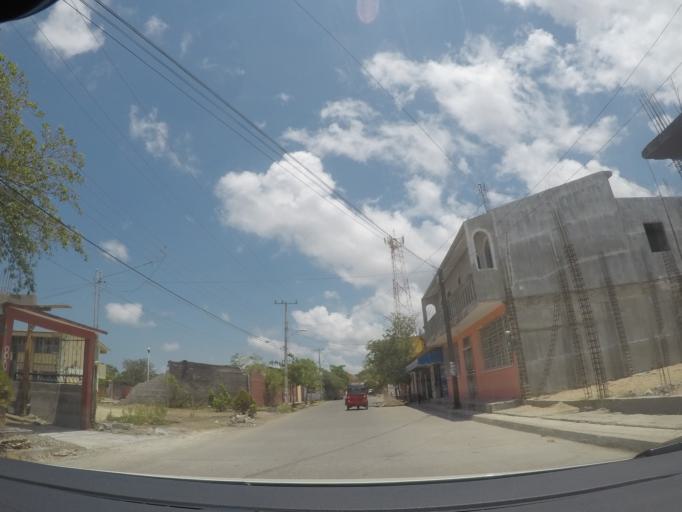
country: MX
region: Oaxaca
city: Juchitan de Zaragoza
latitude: 16.4389
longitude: -95.0132
